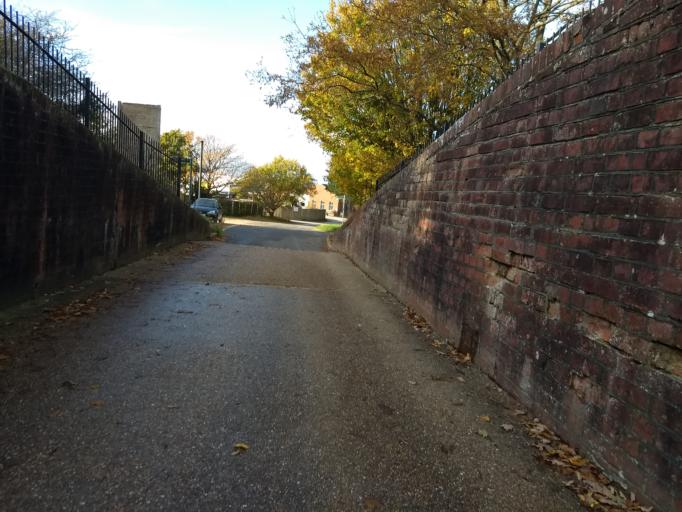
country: GB
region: England
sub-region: Isle of Wight
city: Freshwater
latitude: 50.6898
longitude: -1.5224
